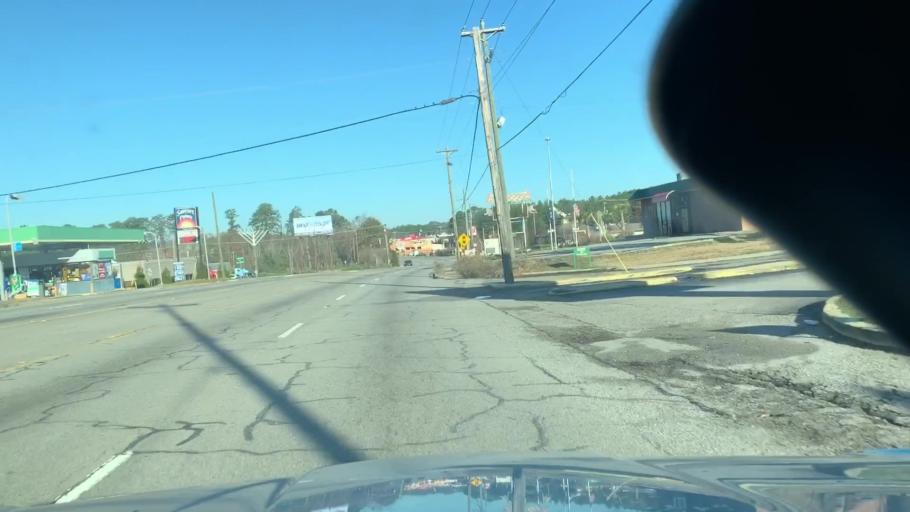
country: US
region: South Carolina
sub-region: Richland County
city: Dentsville
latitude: 34.0578
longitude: -80.9501
